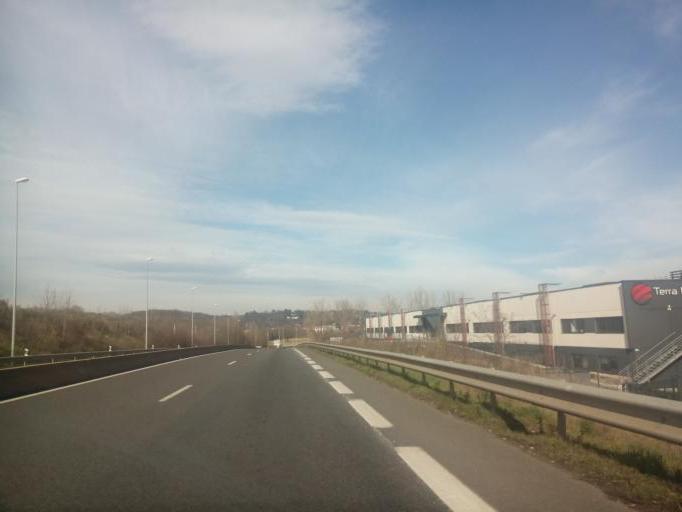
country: FR
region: Rhone-Alpes
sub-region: Departement du Rhone
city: Brignais
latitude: 45.6857
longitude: 4.7664
